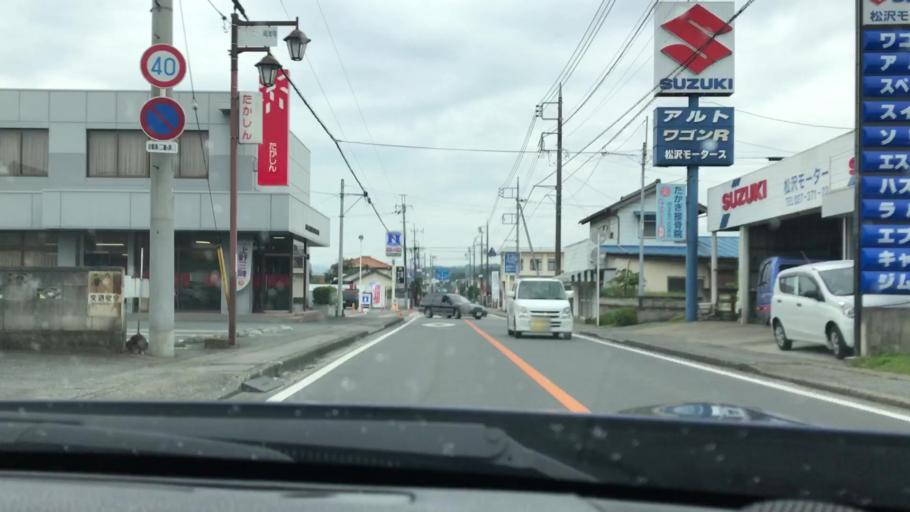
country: JP
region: Gunma
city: Kanekomachi
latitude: 36.3953
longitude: 138.9623
